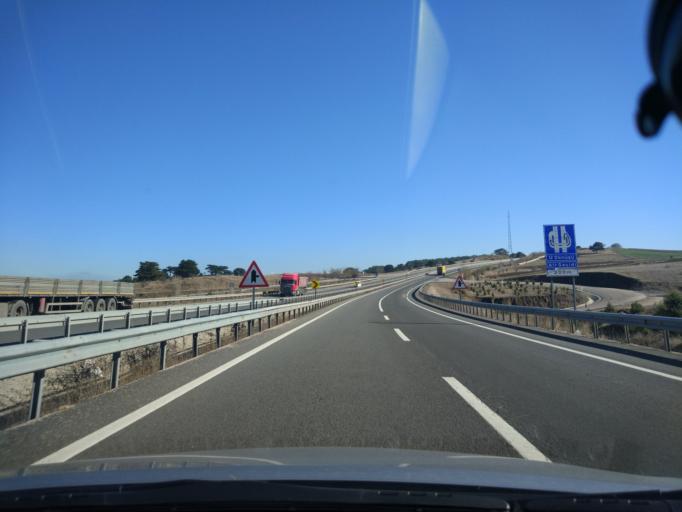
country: TR
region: Karabuk
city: Gozyeri
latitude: 40.8636
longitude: 32.5189
